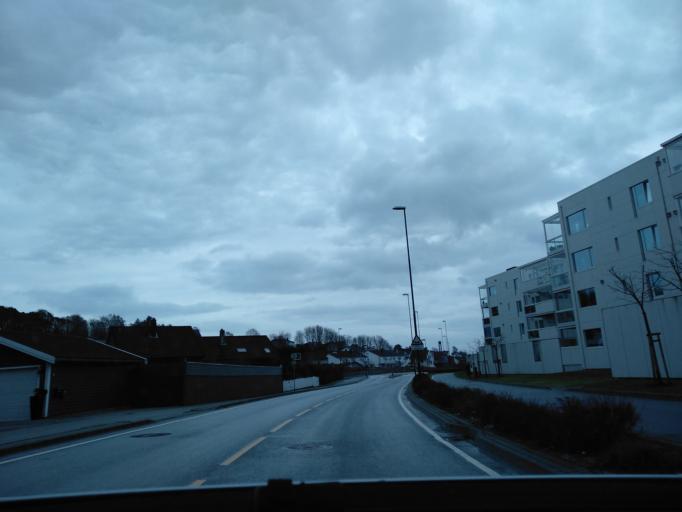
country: NO
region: Rogaland
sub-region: Stavanger
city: Stavanger
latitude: 58.9874
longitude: 5.6931
